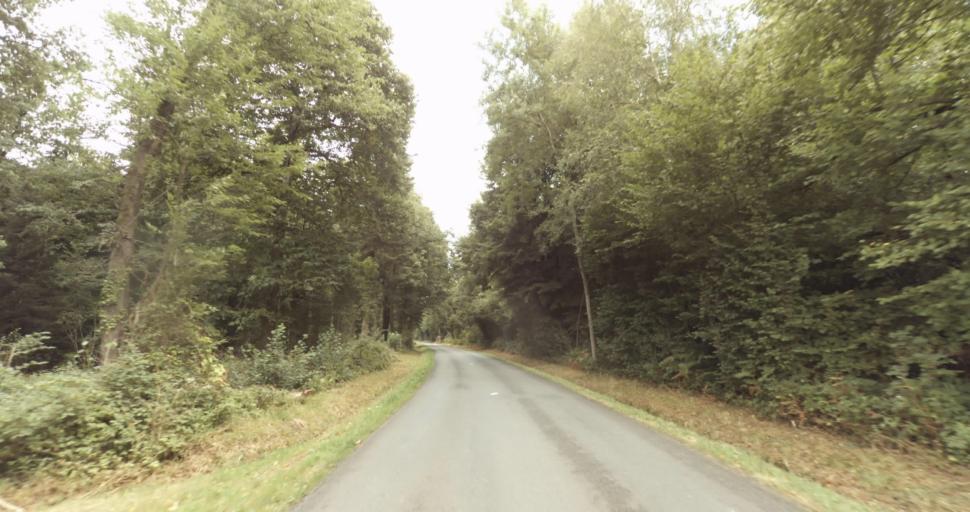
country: FR
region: Lower Normandy
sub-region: Departement de l'Orne
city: Gace
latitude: 48.7985
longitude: 0.2594
